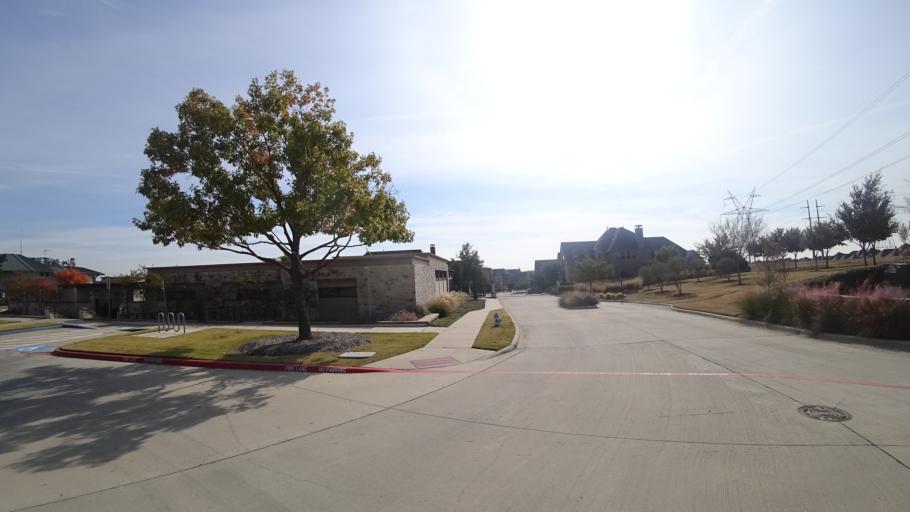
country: US
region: Texas
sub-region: Denton County
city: The Colony
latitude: 33.0417
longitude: -96.9067
